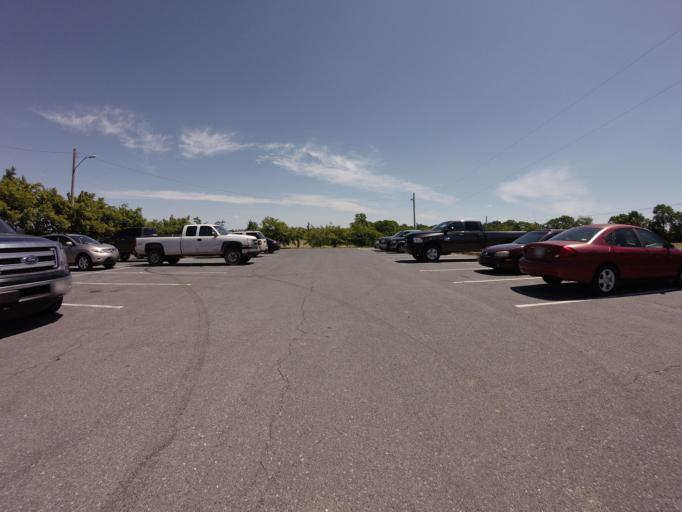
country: US
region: Maryland
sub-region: Frederick County
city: Brunswick
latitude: 39.3406
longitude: -77.6356
